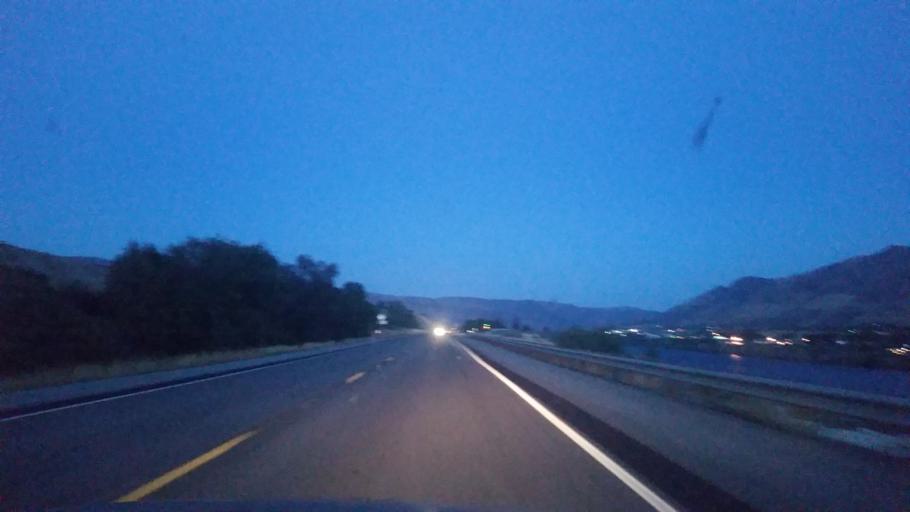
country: US
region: Washington
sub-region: Chelan County
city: South Wenatchee
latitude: 47.3821
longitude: -120.2285
